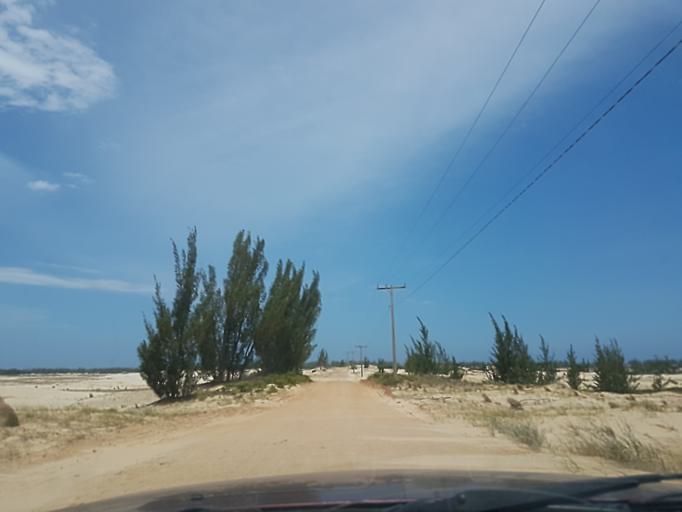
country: BR
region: Santa Catarina
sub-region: Jaguaruna
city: Jaguaruna
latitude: -28.6496
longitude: -48.9614
